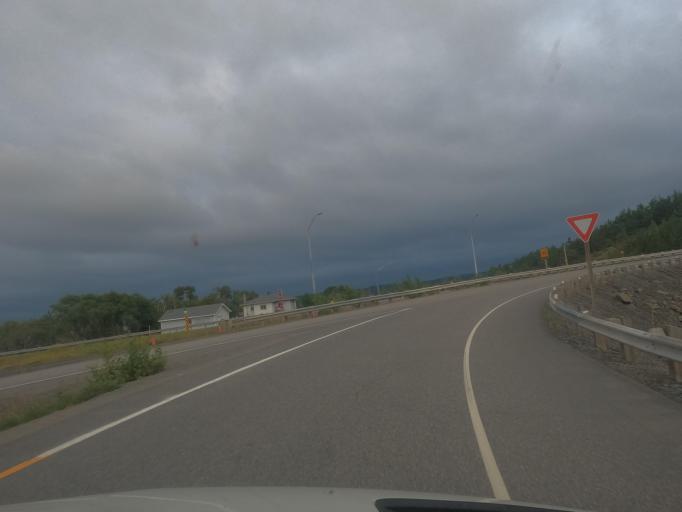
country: CA
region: Ontario
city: Greater Sudbury
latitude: 46.4353
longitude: -80.9668
